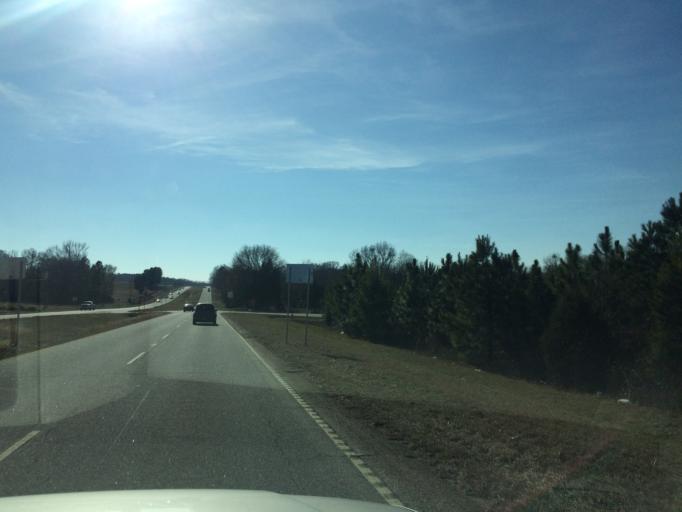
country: US
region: South Carolina
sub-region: Greenwood County
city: Greenwood
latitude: 34.2661
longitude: -82.0826
